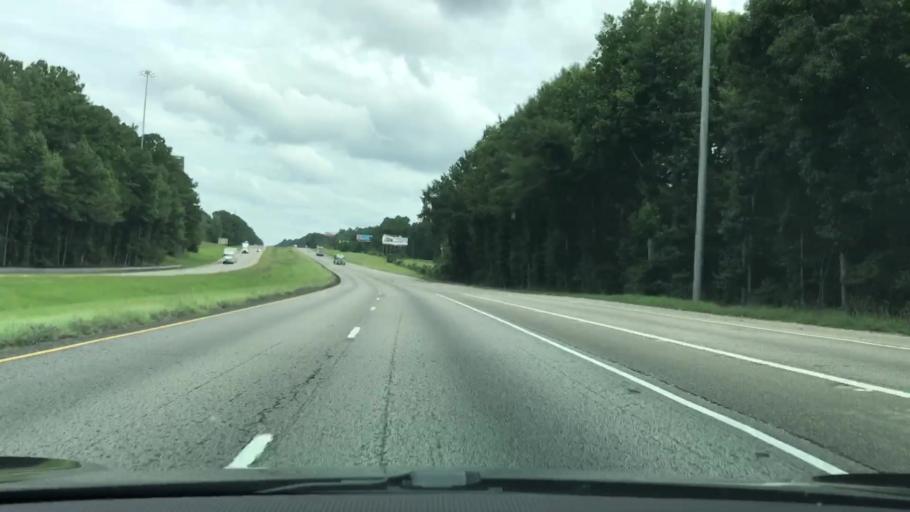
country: US
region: Georgia
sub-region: Troup County
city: West Point
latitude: 32.8805
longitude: -85.1477
